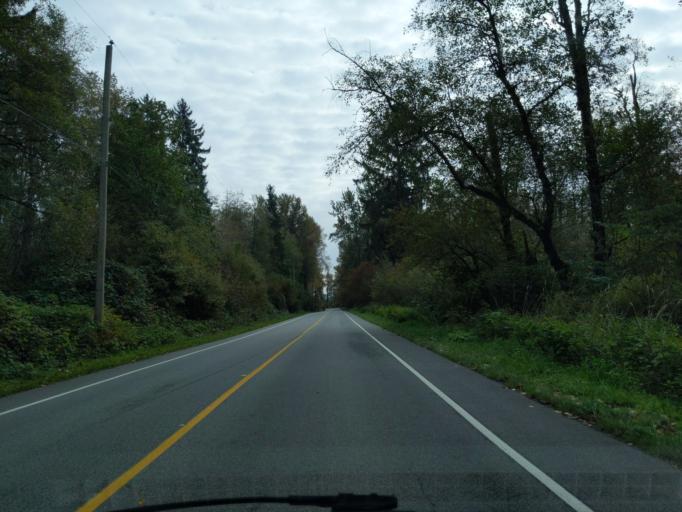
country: CA
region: British Columbia
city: Maple Ridge
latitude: 49.2031
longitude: -122.5990
